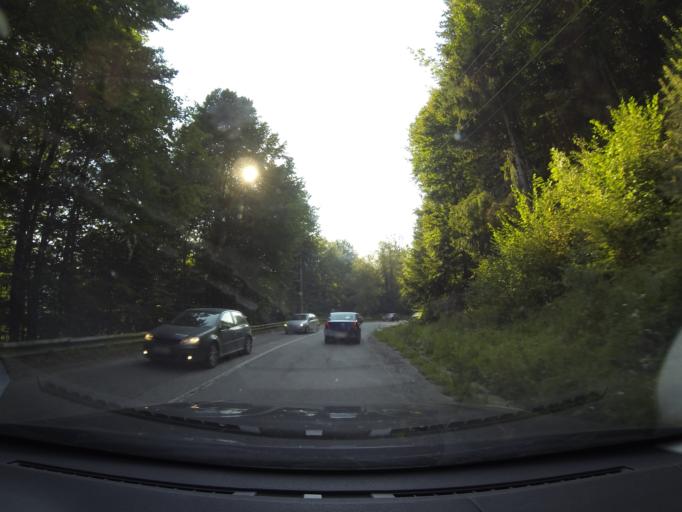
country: RO
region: Arges
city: Poenari
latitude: 45.3711
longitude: 24.6490
